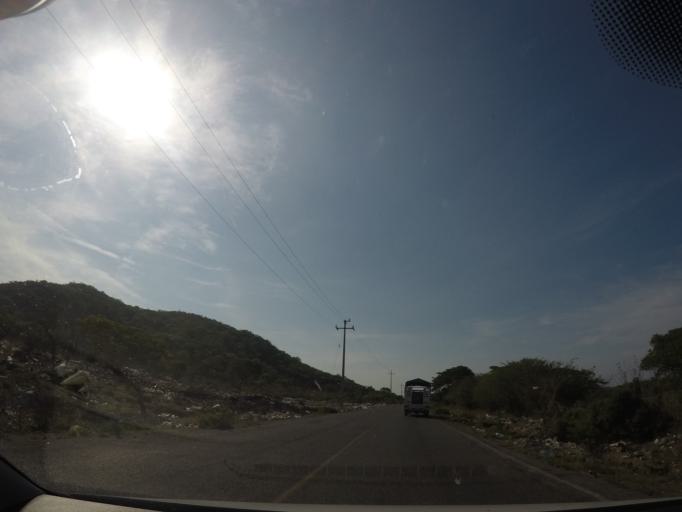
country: MX
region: Oaxaca
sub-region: Salina Cruz
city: Salina Cruz
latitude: 16.2307
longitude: -95.1429
